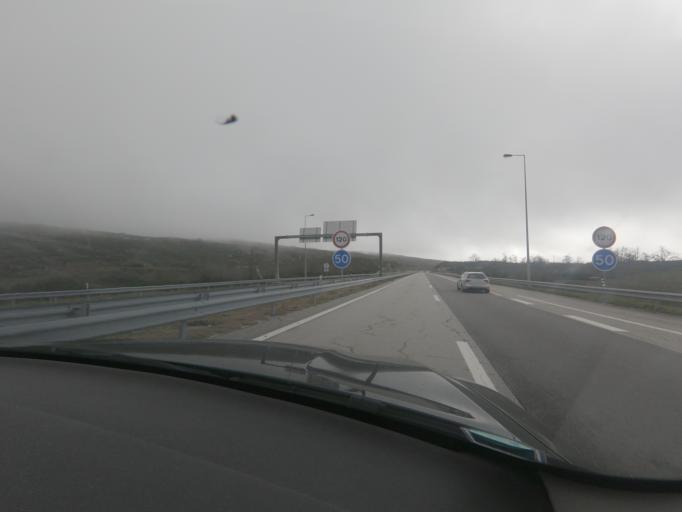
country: PT
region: Viseu
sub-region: Tarouca
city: Tarouca
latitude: 41.0003
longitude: -7.8832
